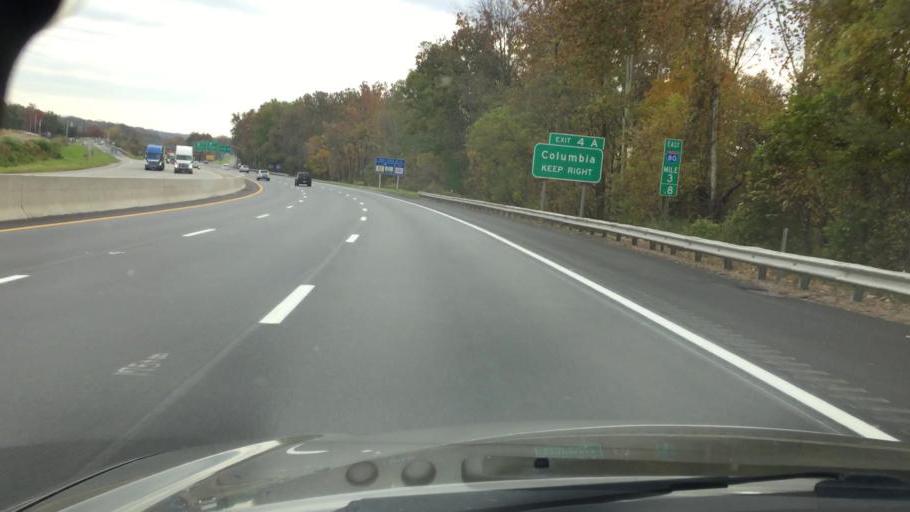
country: US
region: Pennsylvania
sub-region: Northampton County
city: East Bangor
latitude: 40.9344
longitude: -75.1029
